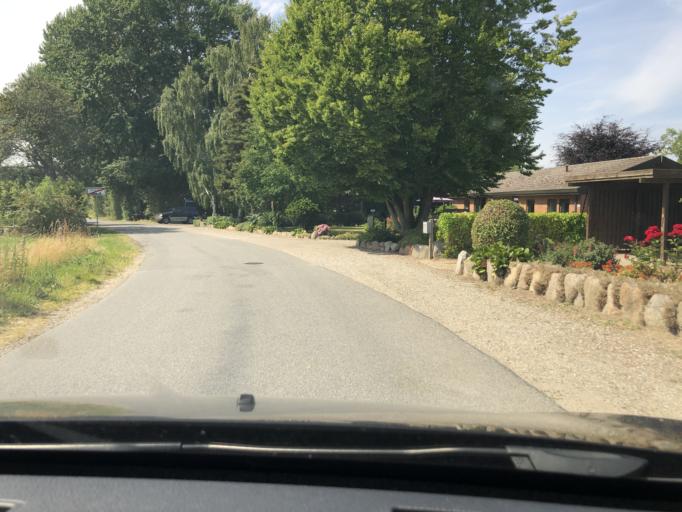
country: DK
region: South Denmark
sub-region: AEro Kommune
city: AEroskobing
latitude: 54.9149
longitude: 10.2956
